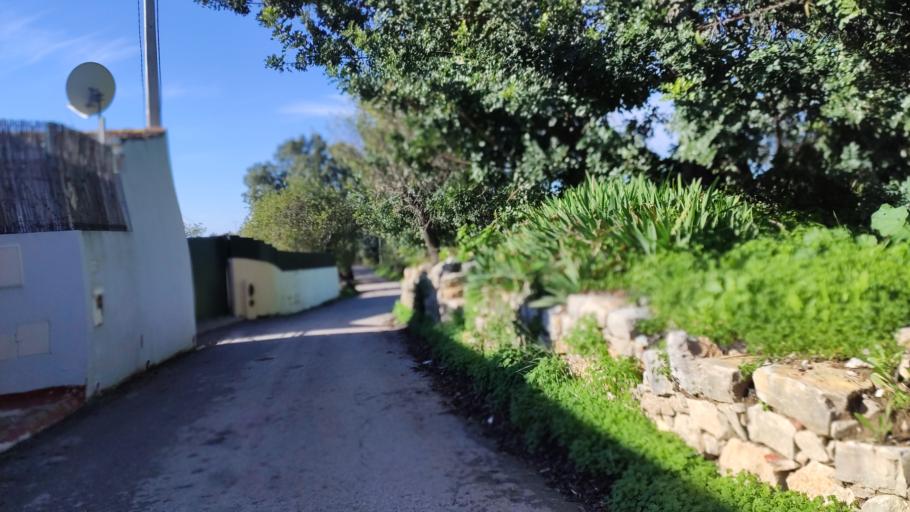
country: PT
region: Faro
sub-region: Sao Bras de Alportel
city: Sao Bras de Alportel
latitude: 37.1501
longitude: -7.8737
